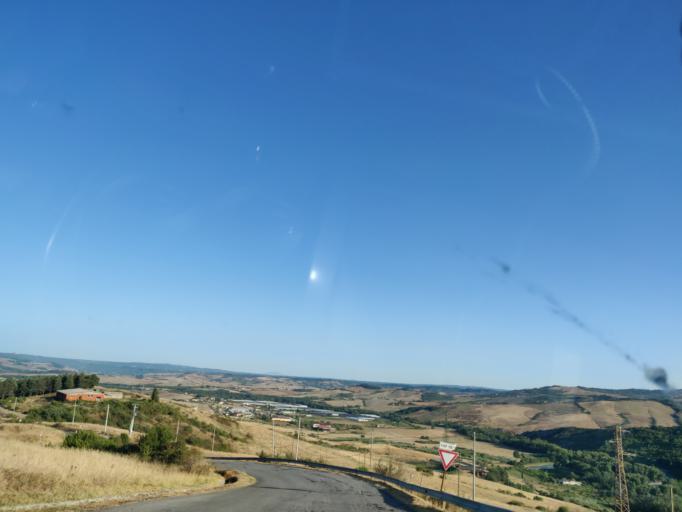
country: IT
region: Tuscany
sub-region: Provincia di Siena
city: Piancastagnaio
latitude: 42.8354
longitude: 11.7104
